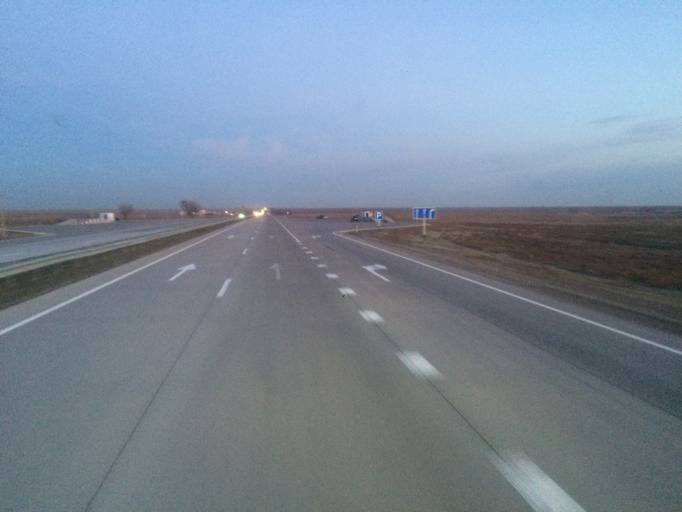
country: KZ
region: Ongtustik Qazaqstan
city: Temirlanovka
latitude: 42.8464
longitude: 69.0926
